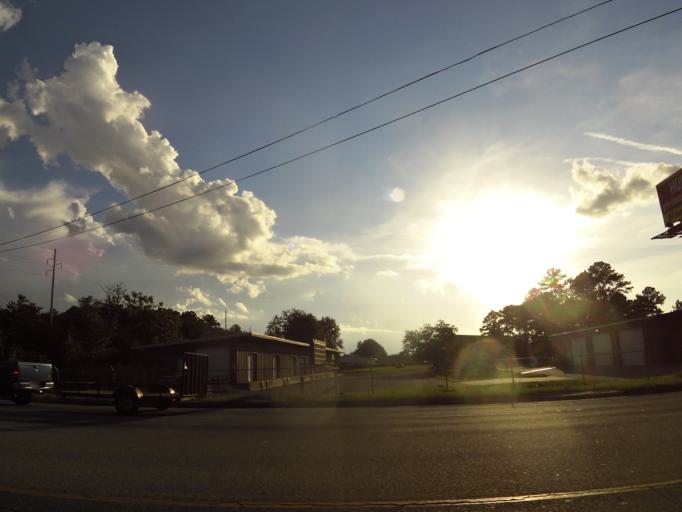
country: US
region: Georgia
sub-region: Lowndes County
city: Remerton
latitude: 30.8209
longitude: -83.3023
